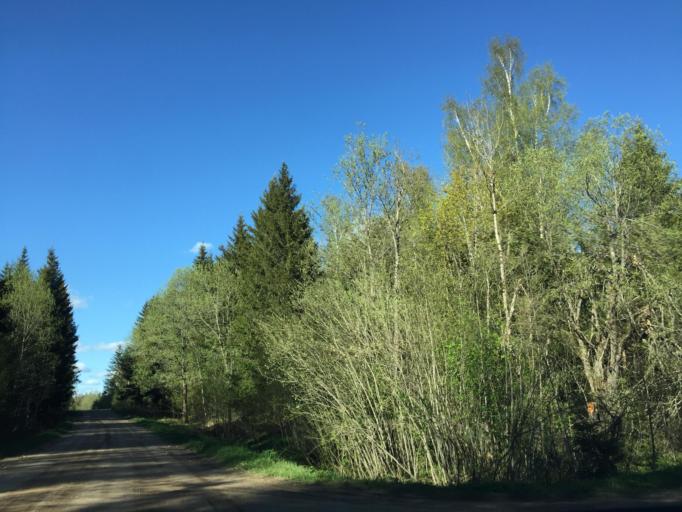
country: LV
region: Vecpiebalga
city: Vecpiebalga
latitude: 56.8593
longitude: 25.9640
